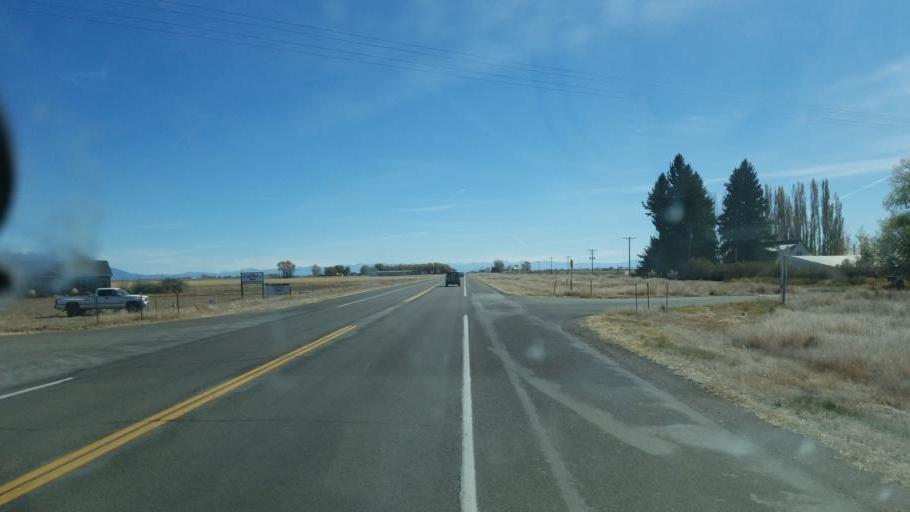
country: US
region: Colorado
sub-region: Rio Grande County
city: Monte Vista
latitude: 37.5520
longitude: -106.0761
